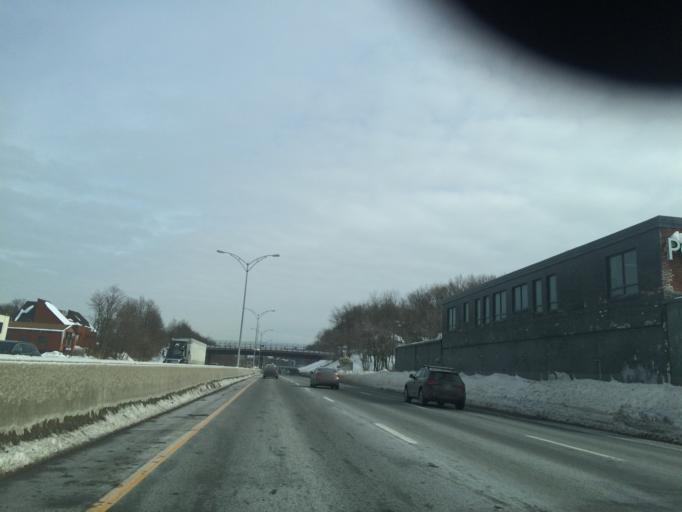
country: US
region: Massachusetts
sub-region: Middlesex County
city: Newton
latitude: 42.3530
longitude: -71.1993
